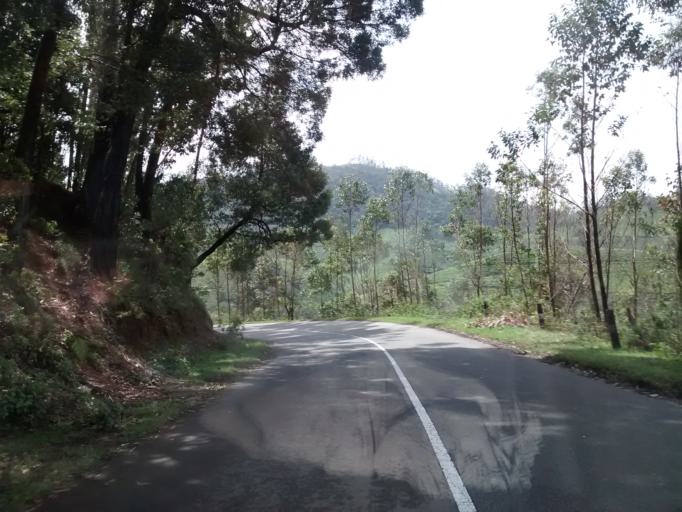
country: IN
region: Kerala
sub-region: Idukki
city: Munnar
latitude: 10.0987
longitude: 77.1132
